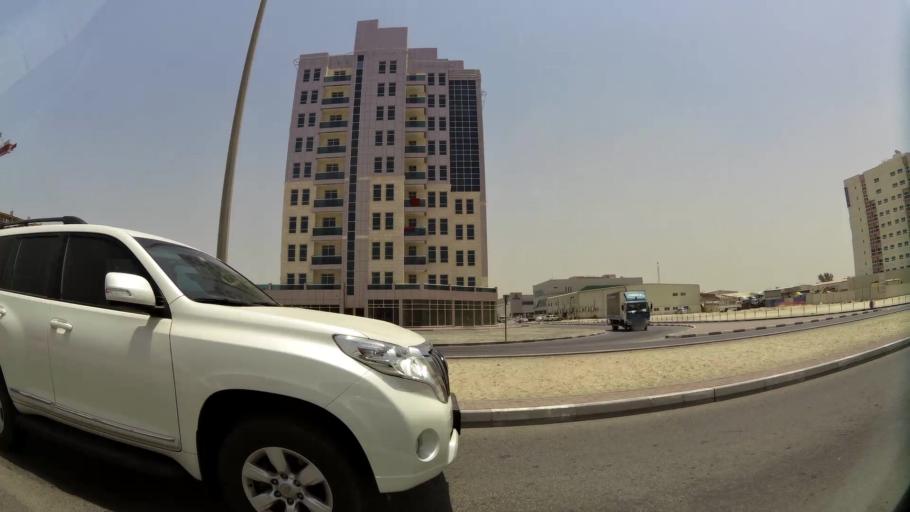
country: AE
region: Ash Shariqah
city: Sharjah
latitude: 25.2850
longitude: 55.4068
